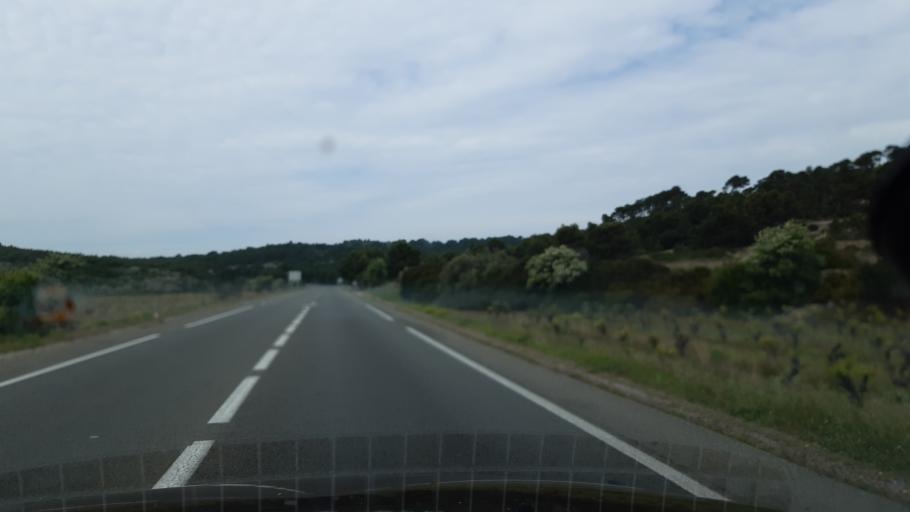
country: FR
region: Languedoc-Roussillon
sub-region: Departement de l'Aude
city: Gruissan
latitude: 43.1180
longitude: 3.0867
